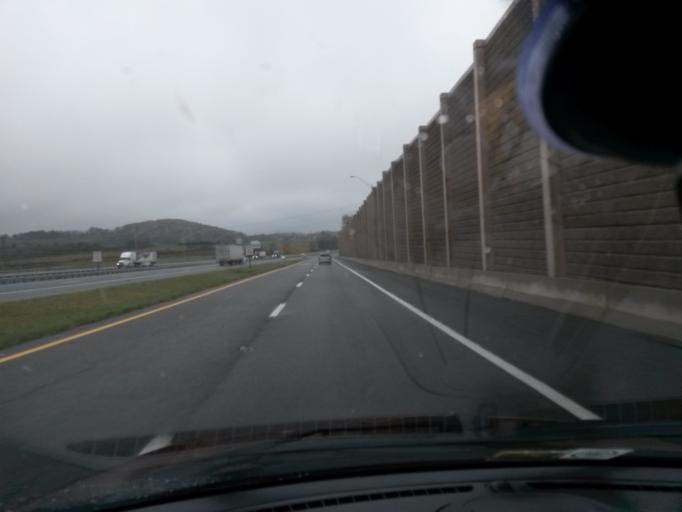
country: US
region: Virginia
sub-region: Montgomery County
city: Christiansburg
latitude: 37.1269
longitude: -80.3774
